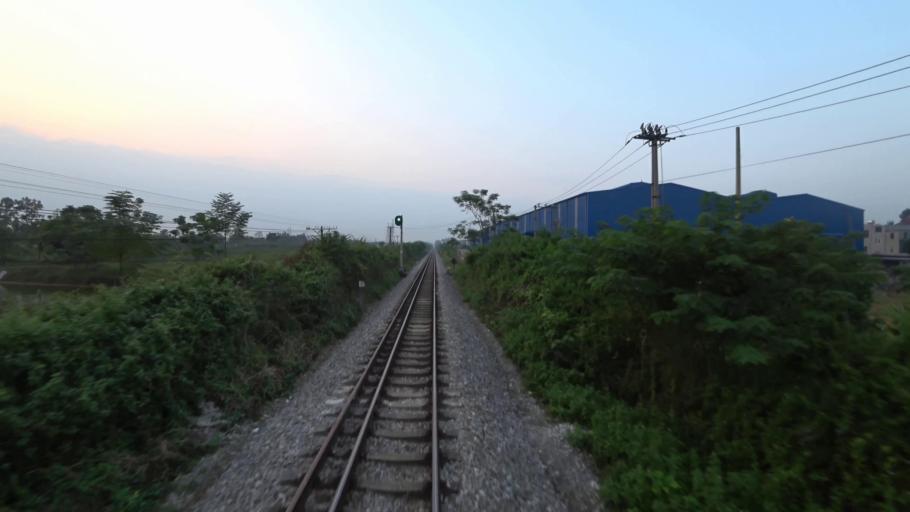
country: VN
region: Ha Noi
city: Dong Anh
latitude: 21.1460
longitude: 105.8604
